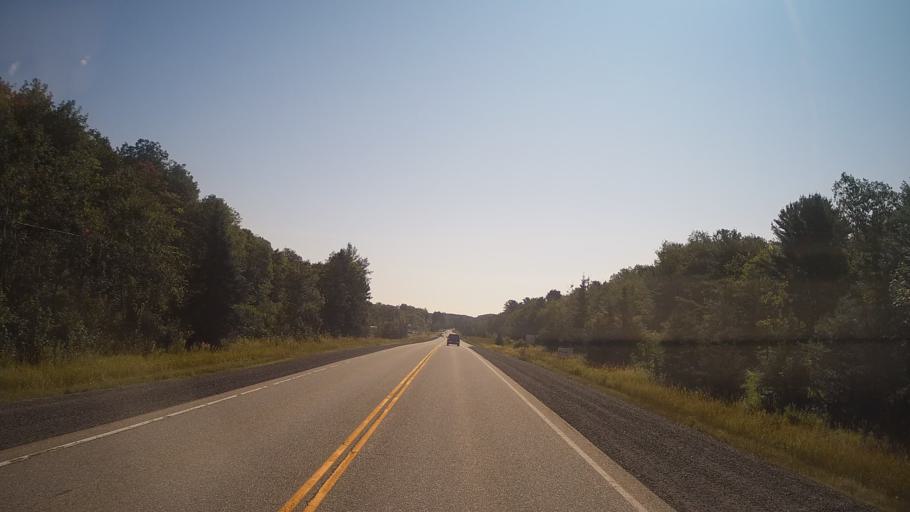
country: CA
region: Ontario
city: Elliot Lake
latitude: 46.2051
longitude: -82.4288
